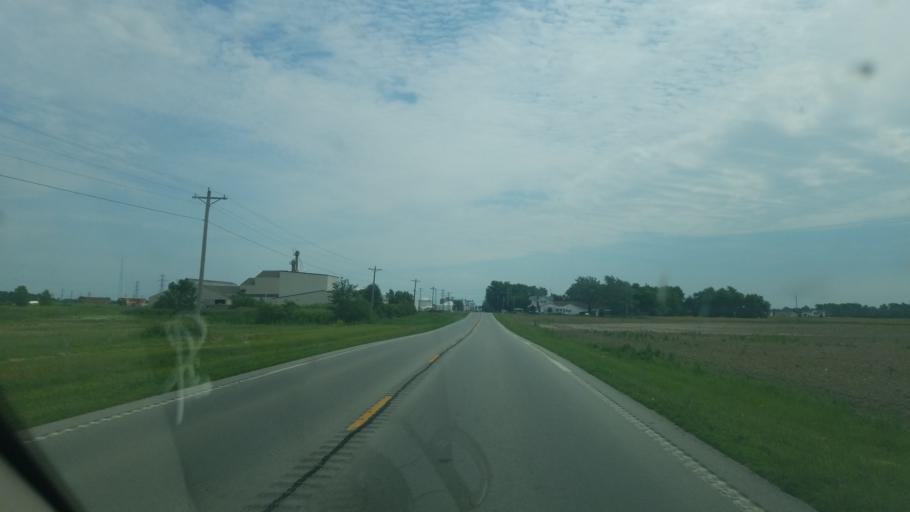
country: US
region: Ohio
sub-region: Seneca County
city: Fostoria
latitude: 41.1388
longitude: -83.4537
